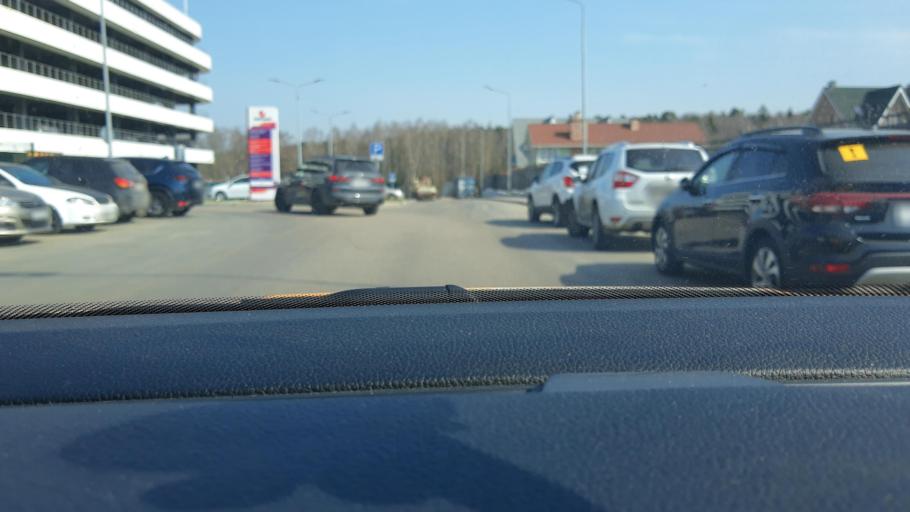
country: RU
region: Moskovskaya
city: Gorki Vtoryye
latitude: 55.6815
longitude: 37.1507
